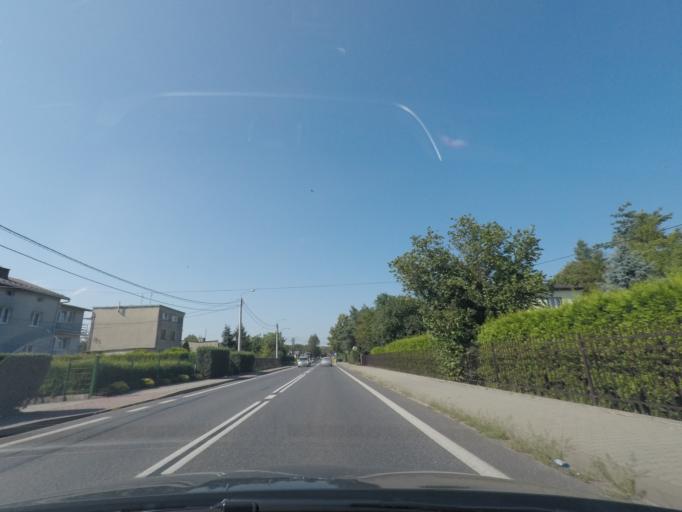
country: PL
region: Lesser Poland Voivodeship
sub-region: Powiat chrzanowski
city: Chrzanow
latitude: 50.1355
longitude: 19.3855
